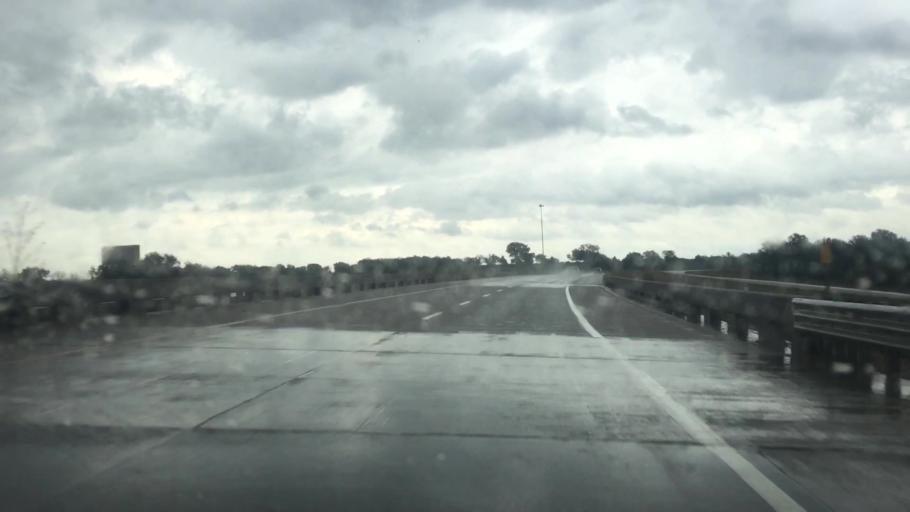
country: US
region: Kansas
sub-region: Miami County
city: Osawatomie
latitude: 38.5106
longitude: -94.9288
